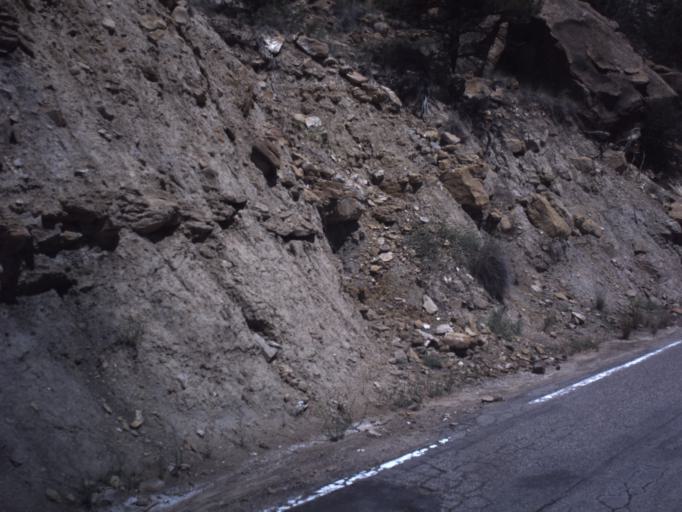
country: US
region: Utah
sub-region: Emery County
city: Orangeville
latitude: 39.2878
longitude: -111.2423
